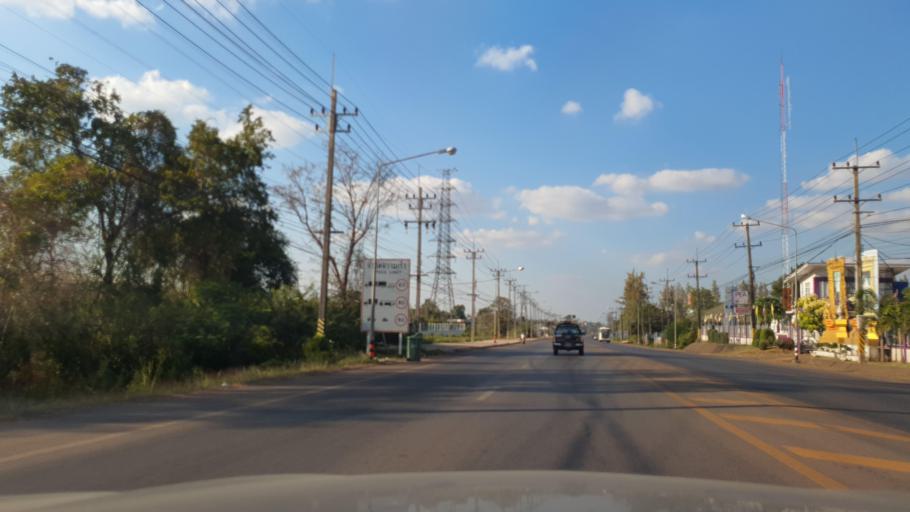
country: TH
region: Sakon Nakhon
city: Sakon Nakhon
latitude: 17.1451
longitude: 104.1093
